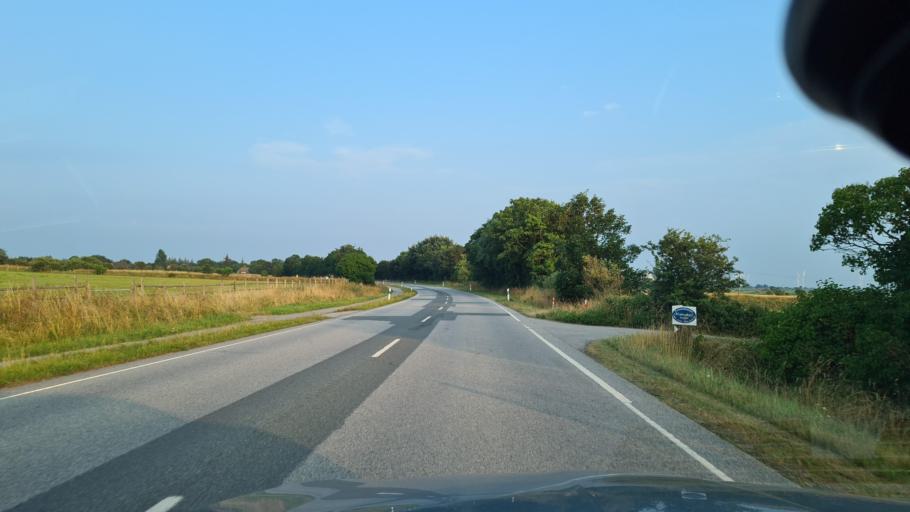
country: DE
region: Schleswig-Holstein
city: Schobull
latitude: 54.4998
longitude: 9.0186
